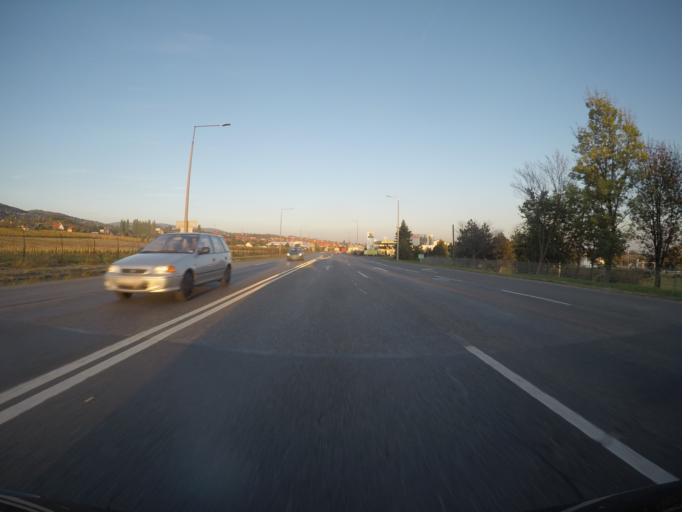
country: HU
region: Baranya
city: Pellerd
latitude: 46.0646
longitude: 18.1592
